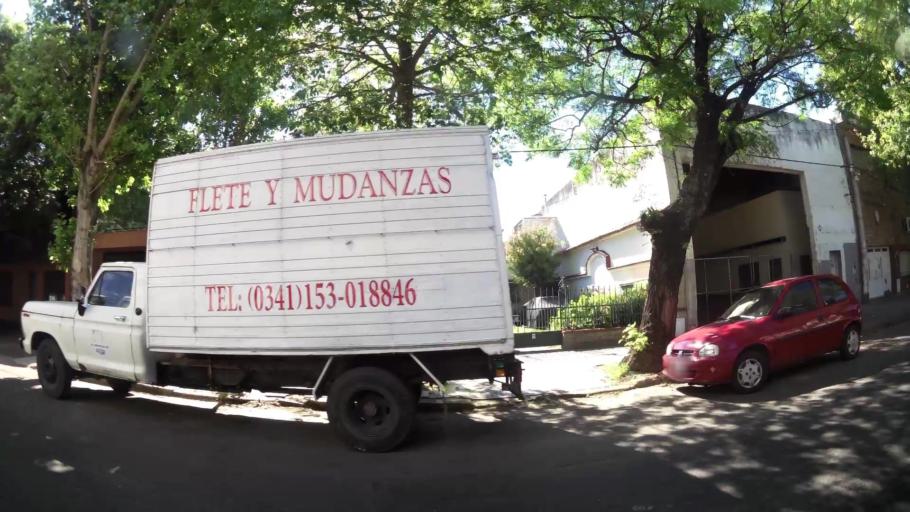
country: AR
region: Santa Fe
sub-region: Departamento de Rosario
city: Rosario
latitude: -32.9494
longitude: -60.6747
